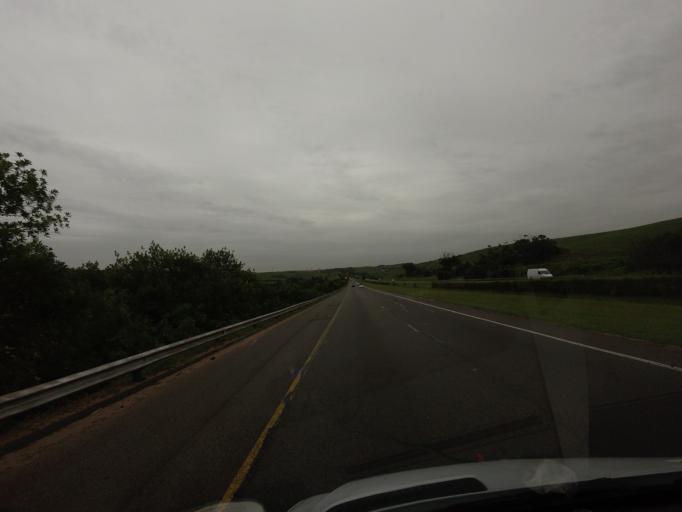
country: ZA
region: KwaZulu-Natal
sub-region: eThekwini Metropolitan Municipality
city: Durban
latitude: -29.6919
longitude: 31.0823
